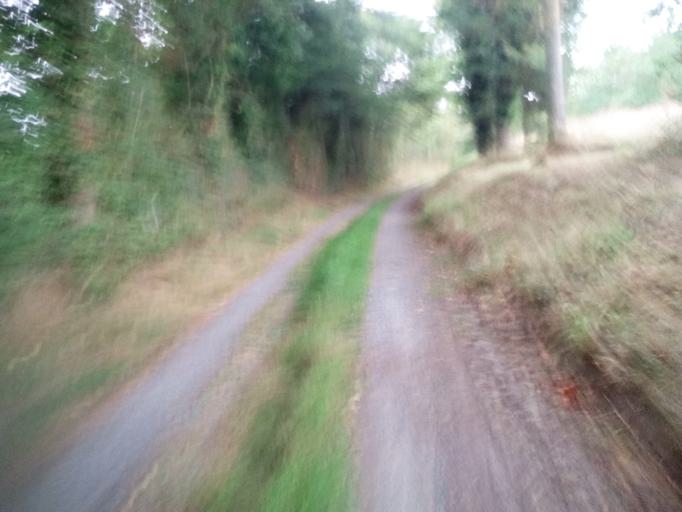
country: FR
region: Lower Normandy
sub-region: Departement du Calvados
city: Bavent
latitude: 49.2348
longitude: -0.1530
